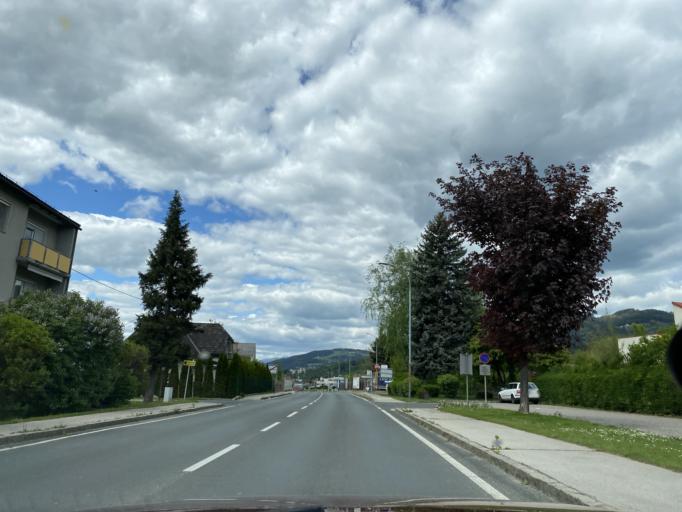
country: AT
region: Carinthia
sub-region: Politischer Bezirk Wolfsberg
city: Wolfsberg
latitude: 46.8146
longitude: 14.8507
